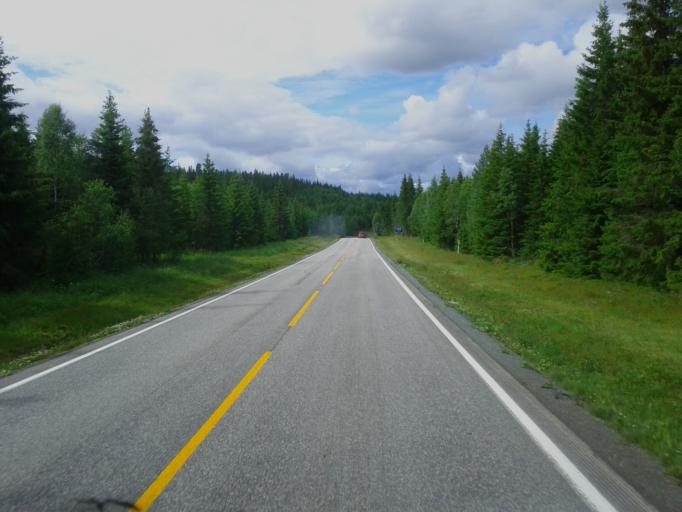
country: NO
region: Nord-Trondelag
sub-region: Hoylandet
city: Hoylandet
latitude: 64.6657
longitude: 12.6731
